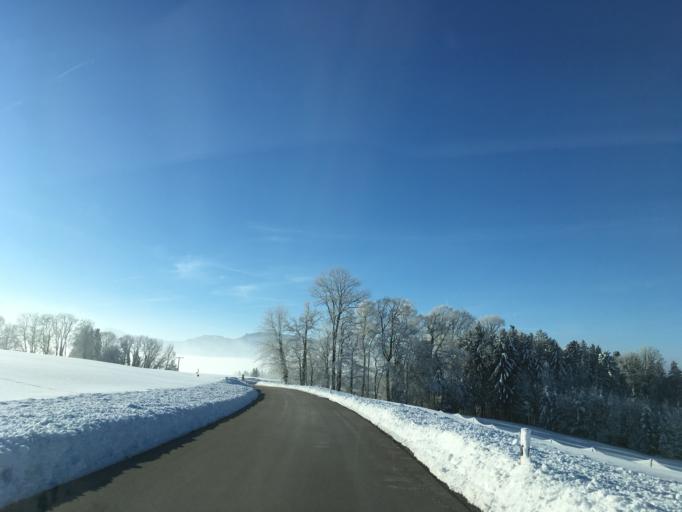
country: DE
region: Bavaria
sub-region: Upper Bavaria
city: Bad Endorf
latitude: 47.8694
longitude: 12.2892
